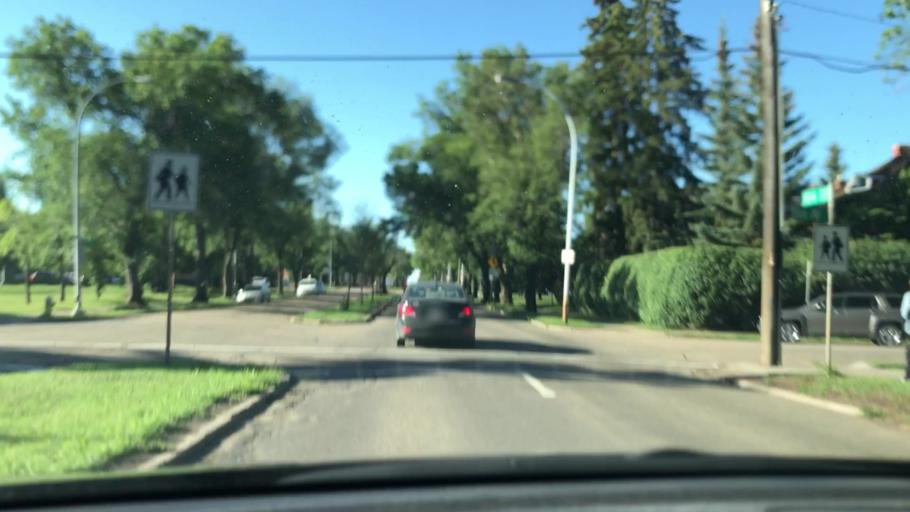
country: CA
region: Alberta
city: Edmonton
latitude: 53.5221
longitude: -113.4976
